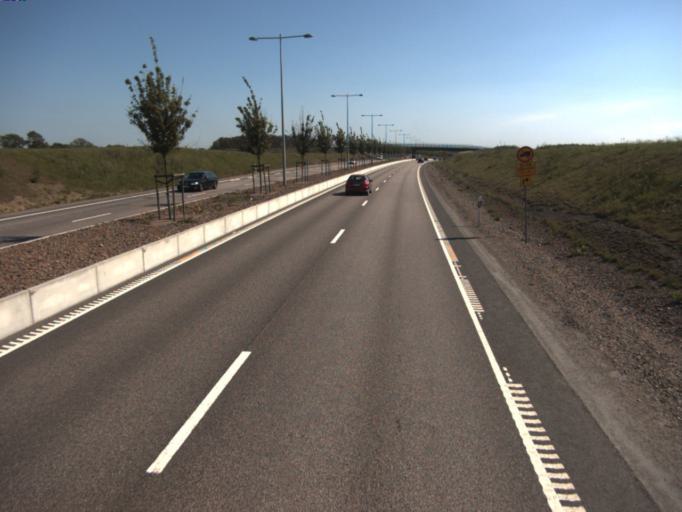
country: SE
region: Skane
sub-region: Helsingborg
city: Gantofta
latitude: 56.0327
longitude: 12.7613
